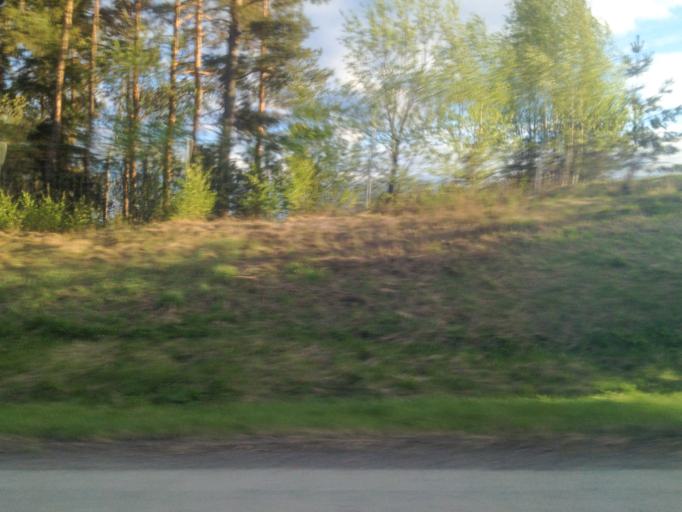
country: FI
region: Pirkanmaa
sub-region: Etelae-Pirkanmaa
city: Akaa
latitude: 61.1910
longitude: 23.8683
